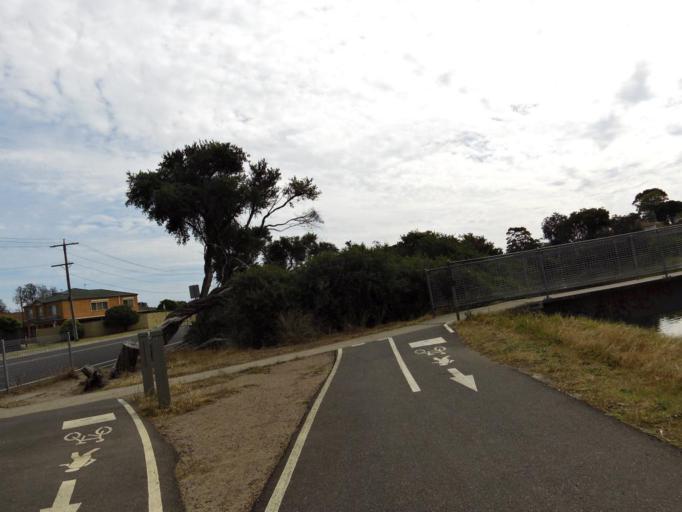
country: AU
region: Victoria
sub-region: Kingston
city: Carrum
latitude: -38.0834
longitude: 145.1336
